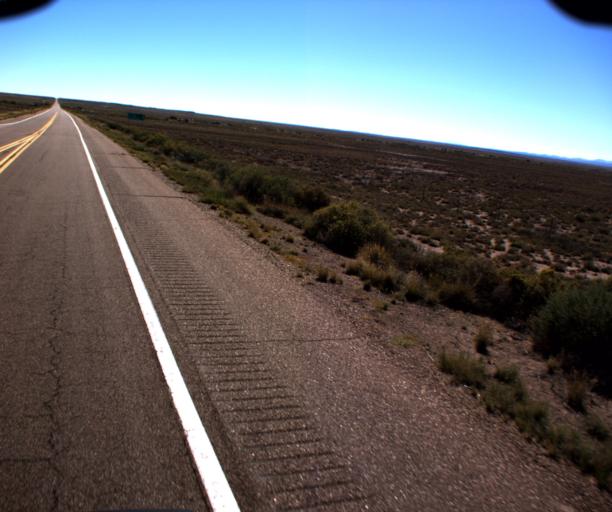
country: US
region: Arizona
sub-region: Navajo County
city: Holbrook
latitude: 34.7910
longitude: -109.8916
